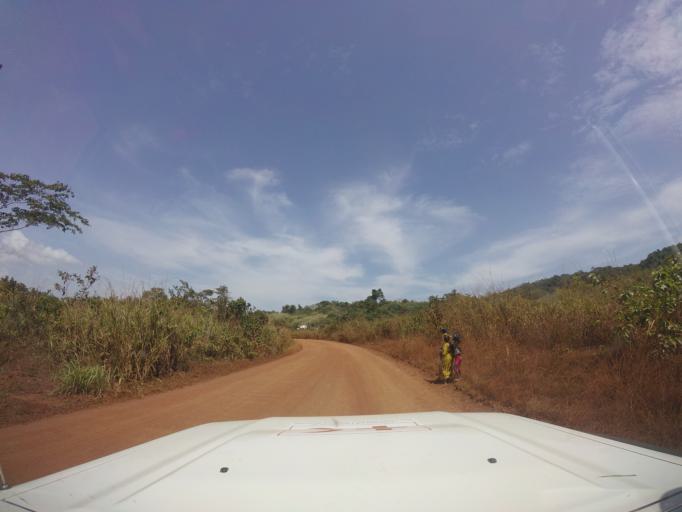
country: LR
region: Grand Cape Mount
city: Robertsport
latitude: 6.7469
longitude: -11.3517
